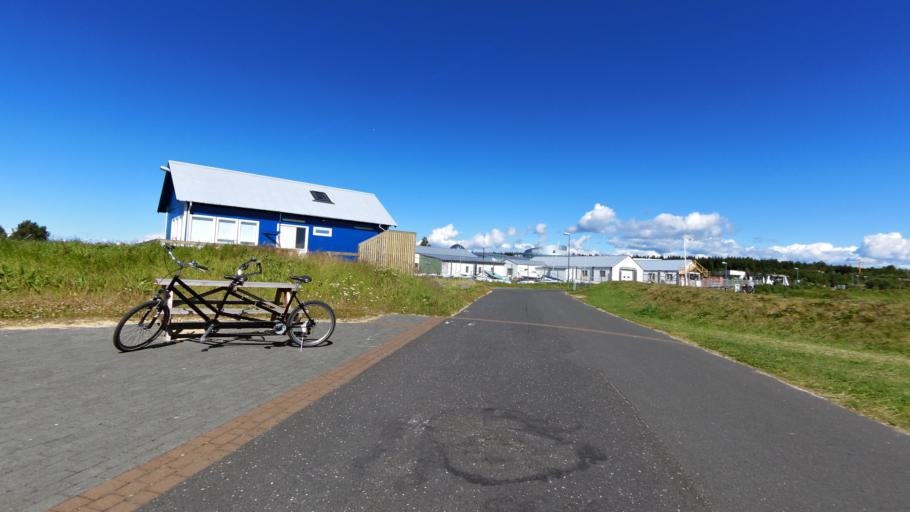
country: IS
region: Capital Region
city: Kopavogur
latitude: 64.1217
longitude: -21.9321
